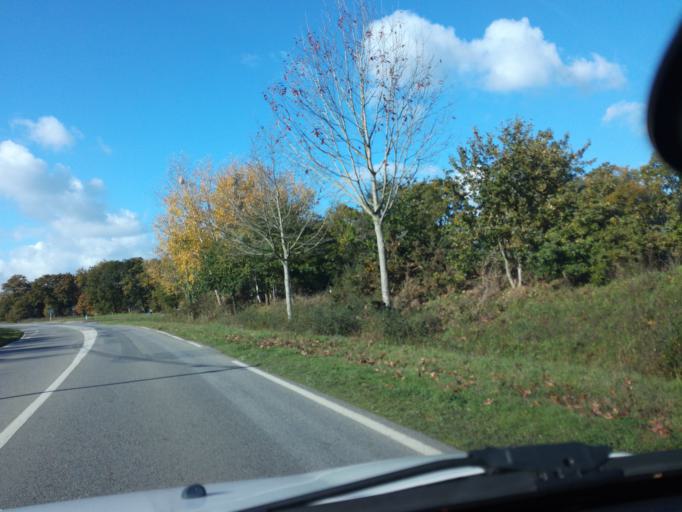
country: FR
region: Brittany
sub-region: Departement d'Ille-et-Vilaine
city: Chavagne
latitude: 48.0262
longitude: -1.7853
